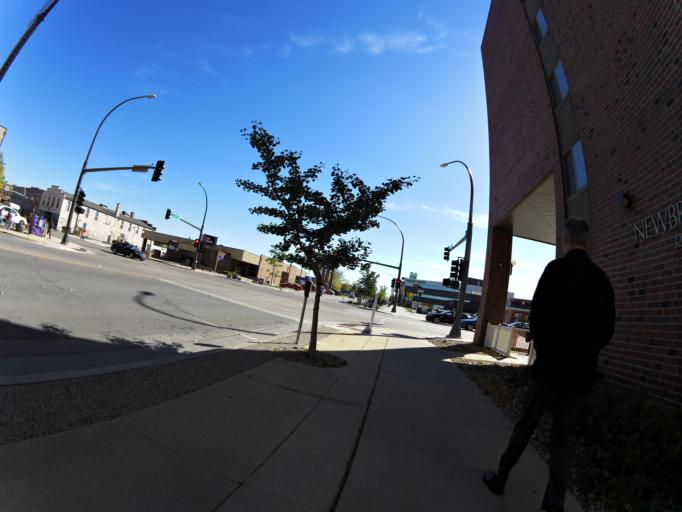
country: US
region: Minnesota
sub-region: Olmsted County
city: Rochester
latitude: 44.0409
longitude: -92.4161
